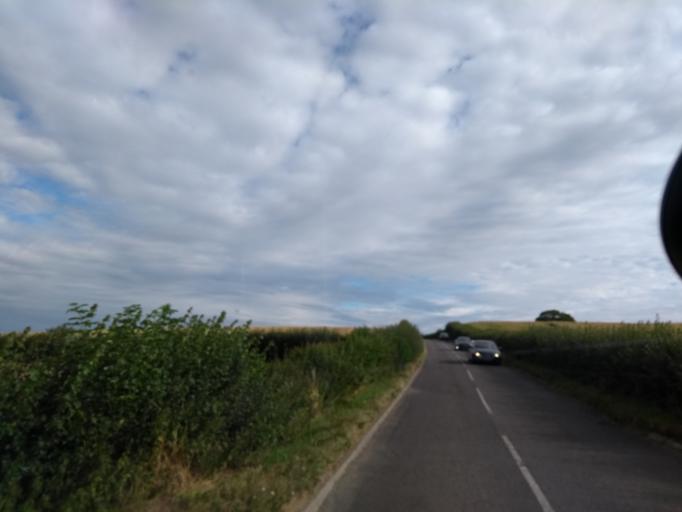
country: GB
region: England
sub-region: Somerset
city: Ilminster
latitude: 50.9076
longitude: -2.8647
